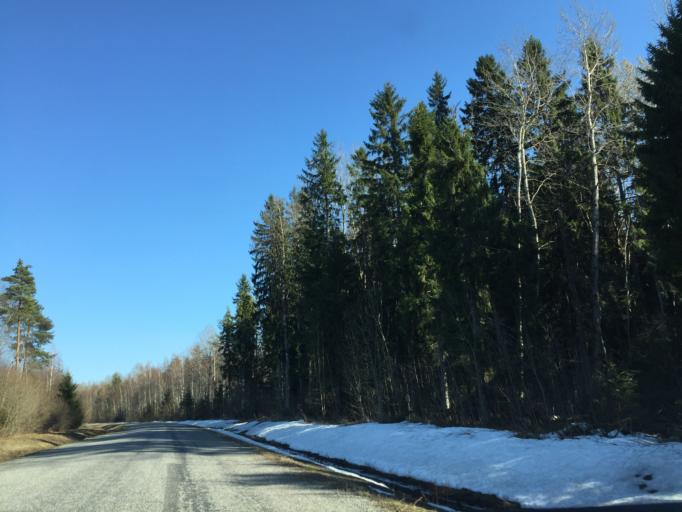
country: RU
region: Pskov
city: Gdov
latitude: 59.0109
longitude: 27.6121
